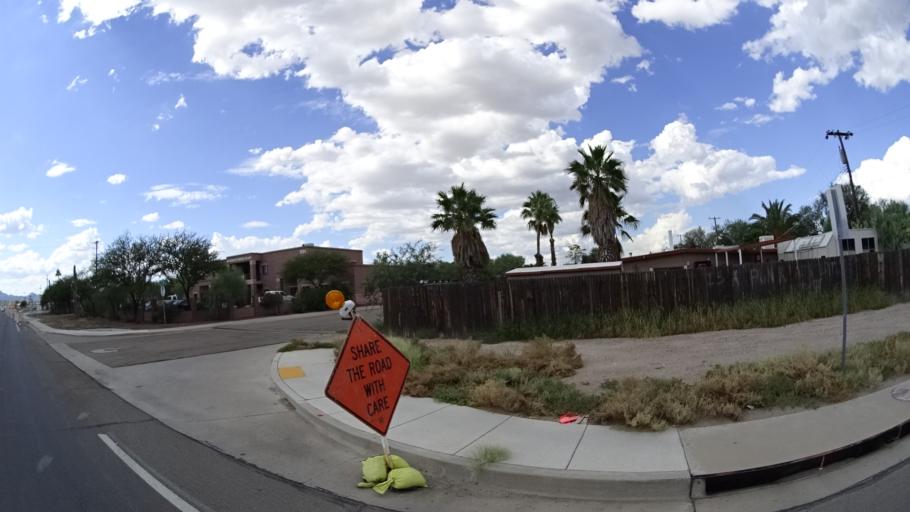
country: US
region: Arizona
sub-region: Pima County
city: Flowing Wells
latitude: 32.2943
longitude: -111.0210
